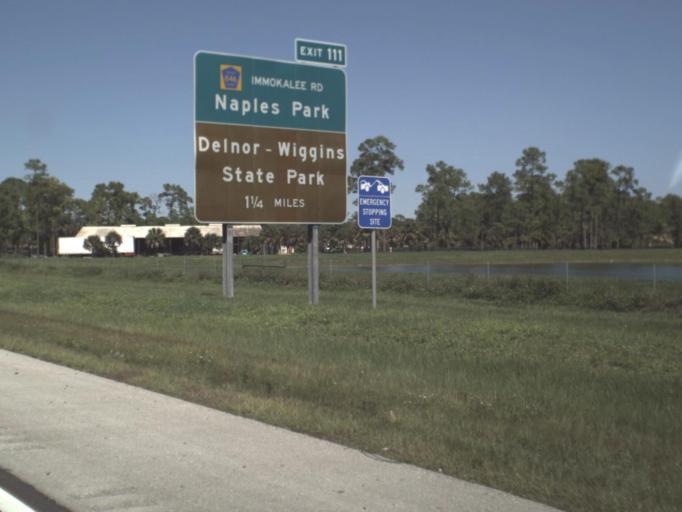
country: US
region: Florida
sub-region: Collier County
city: Vineyards
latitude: 26.2521
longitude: -81.7388
